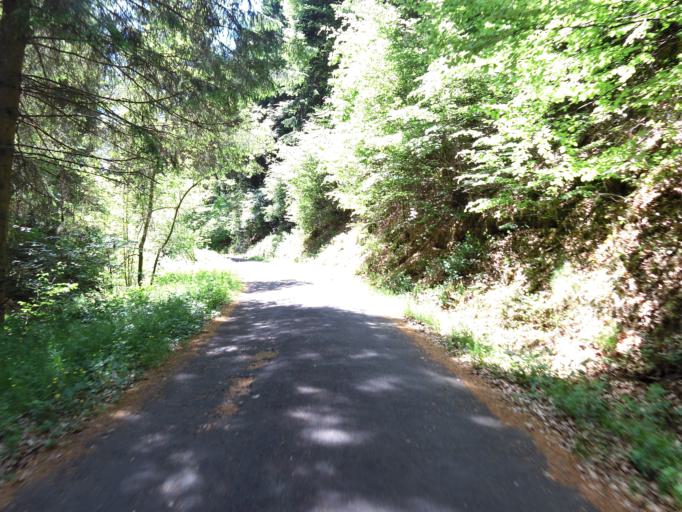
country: DE
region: Rheinland-Pfalz
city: Fischbach
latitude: 49.4199
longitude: 7.9395
